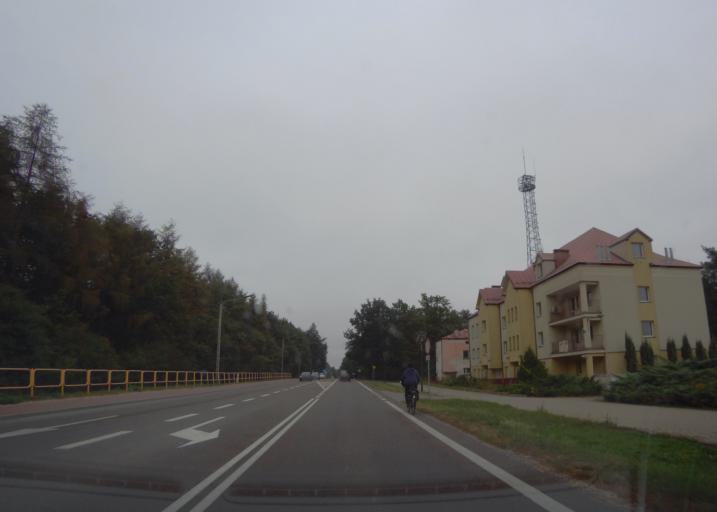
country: PL
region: Lublin Voivodeship
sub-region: Powiat krasnostawski
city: Krasnystaw
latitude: 50.9975
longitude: 23.1873
